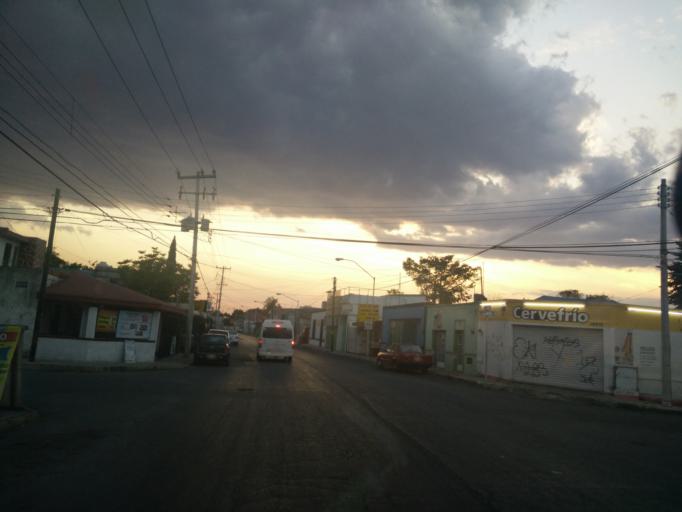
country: MX
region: Yucatan
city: Merida
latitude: 20.9638
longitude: -89.6384
